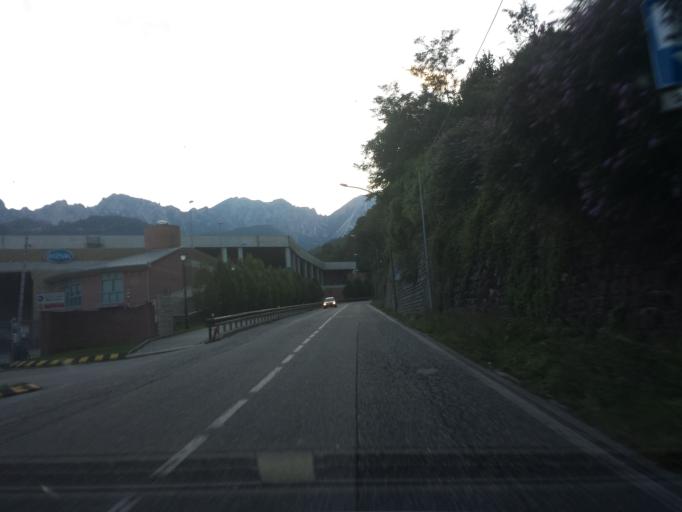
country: IT
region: Veneto
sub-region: Provincia di Vicenza
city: Recoaro Terme
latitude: 45.7066
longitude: 11.2344
